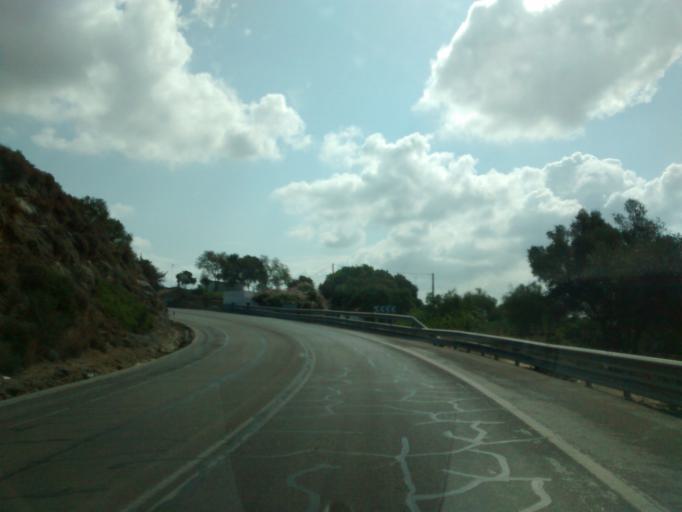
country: ES
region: Andalusia
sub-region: Provincia de Cadiz
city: Vejer de la Frontera
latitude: 36.2521
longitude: -5.9531
